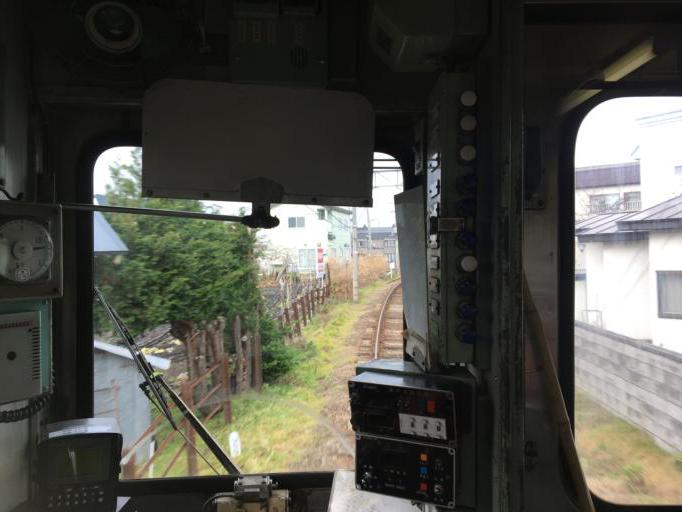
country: JP
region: Aomori
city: Hirosaki
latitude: 40.5682
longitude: 140.4790
